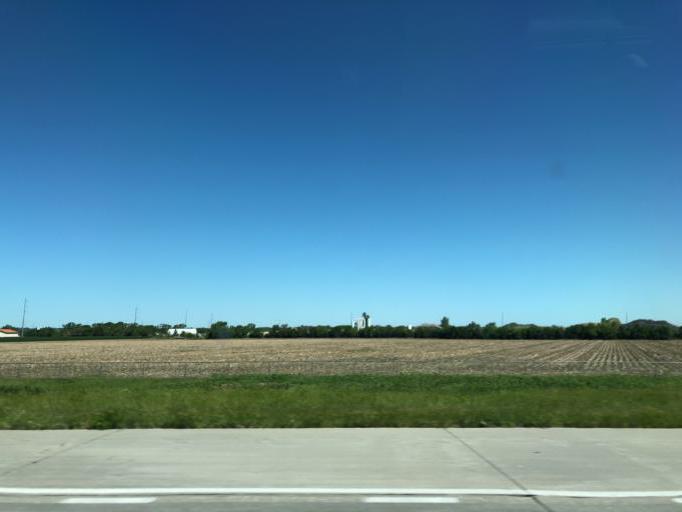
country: US
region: Nebraska
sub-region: Lancaster County
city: Waverly
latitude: 40.8970
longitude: -96.5496
